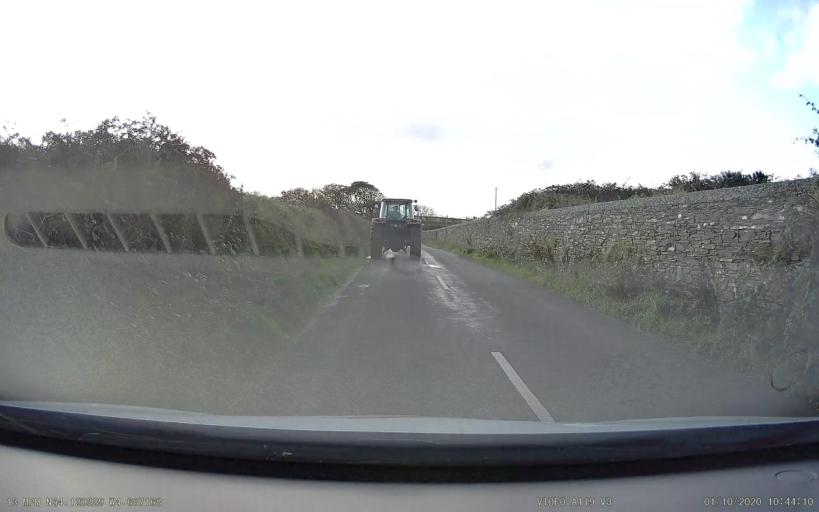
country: IM
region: Castletown
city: Castletown
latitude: 54.1203
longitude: -4.6872
